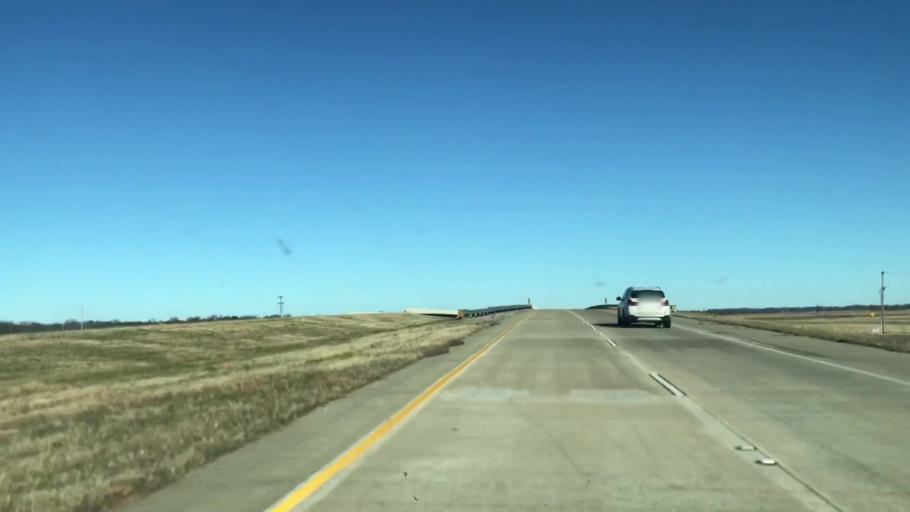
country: US
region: Louisiana
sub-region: Caddo Parish
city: Oil City
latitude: 32.7008
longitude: -93.8607
